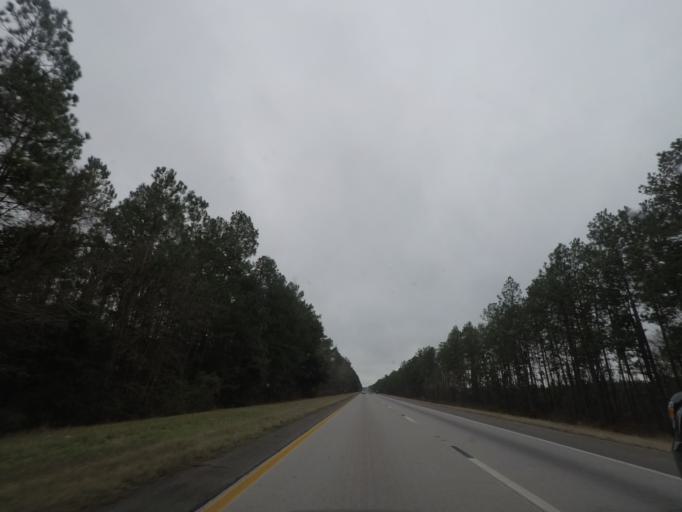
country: US
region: South Carolina
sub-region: Dorchester County
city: Saint George
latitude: 33.0703
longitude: -80.6598
